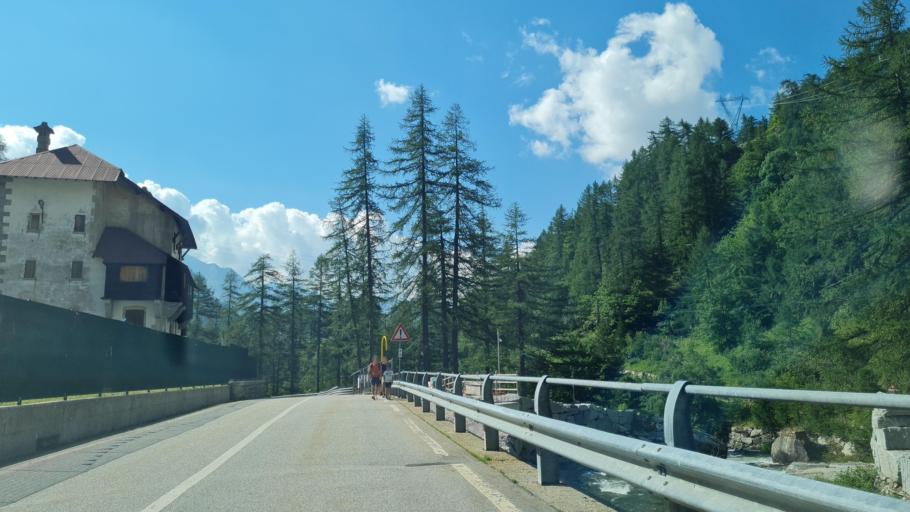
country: IT
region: Piedmont
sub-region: Provincia Verbano-Cusio-Ossola
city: Formazza
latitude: 46.4027
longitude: 8.4177
